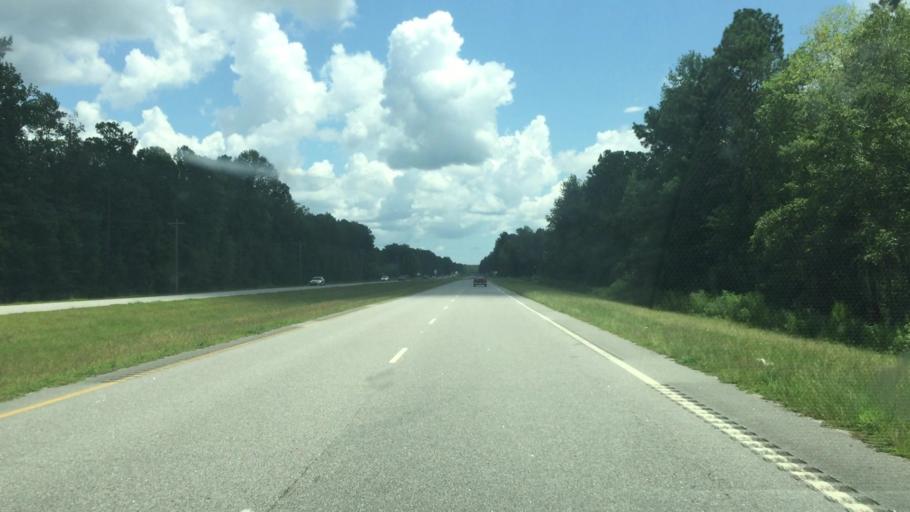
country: US
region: South Carolina
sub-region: Horry County
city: Loris
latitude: 34.0425
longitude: -78.8248
